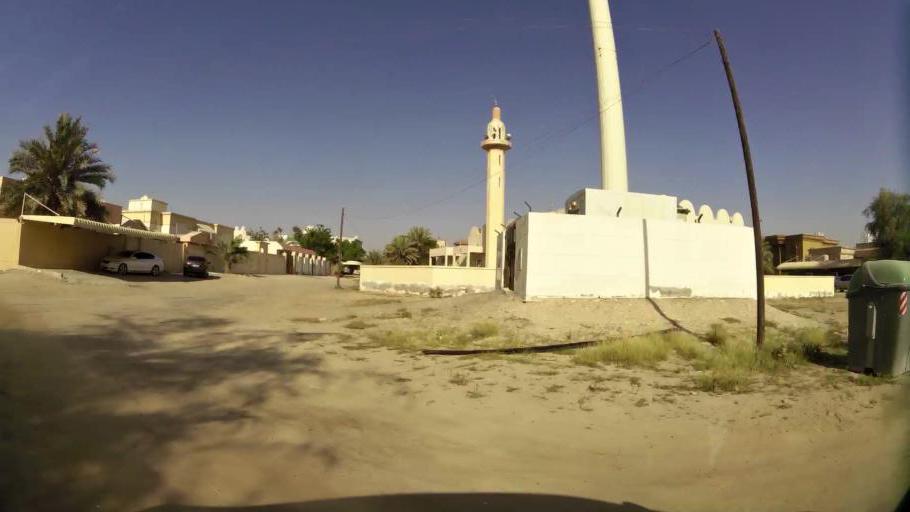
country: AE
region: Ajman
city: Ajman
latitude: 25.4027
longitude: 55.4642
